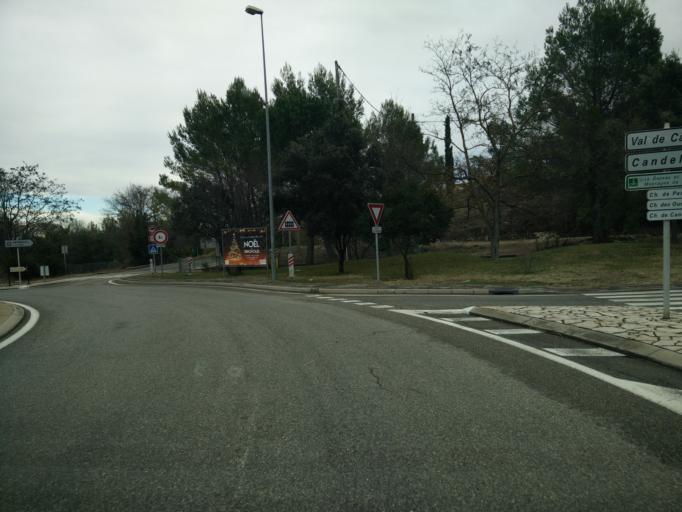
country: FR
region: Provence-Alpes-Cote d'Azur
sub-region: Departement du Var
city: La Celle
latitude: 43.3957
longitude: 6.0462
